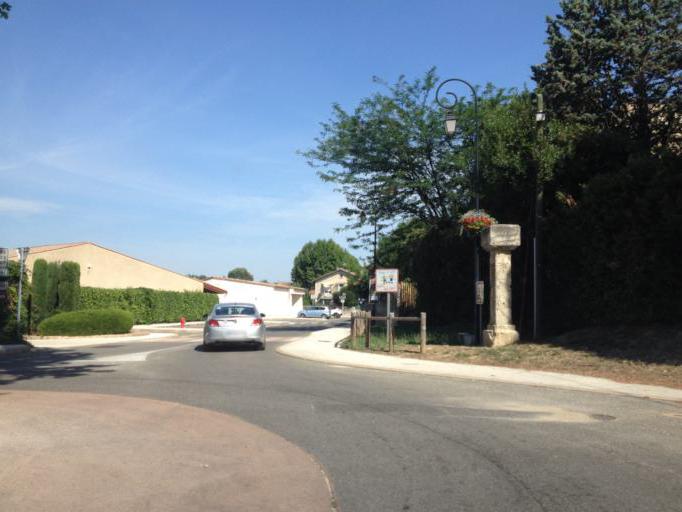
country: FR
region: Provence-Alpes-Cote d'Azur
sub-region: Departement du Vaucluse
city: Mornas
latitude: 44.1999
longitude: 4.7311
